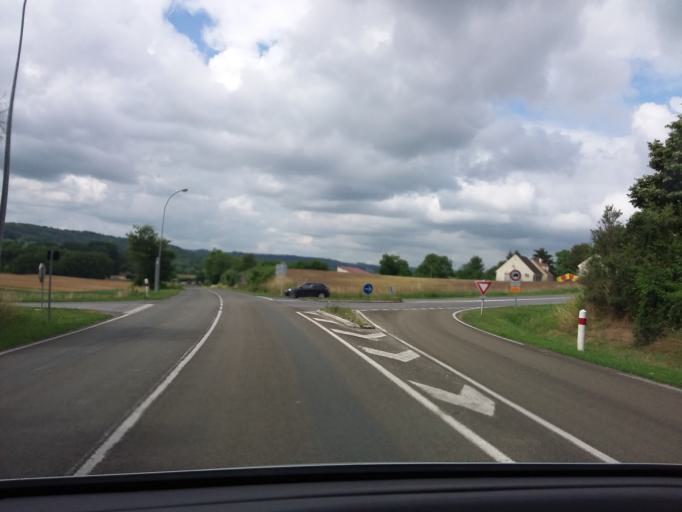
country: FR
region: Picardie
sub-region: Departement de l'Aisne
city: Bucy-le-Long
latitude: 49.3875
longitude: 3.4439
